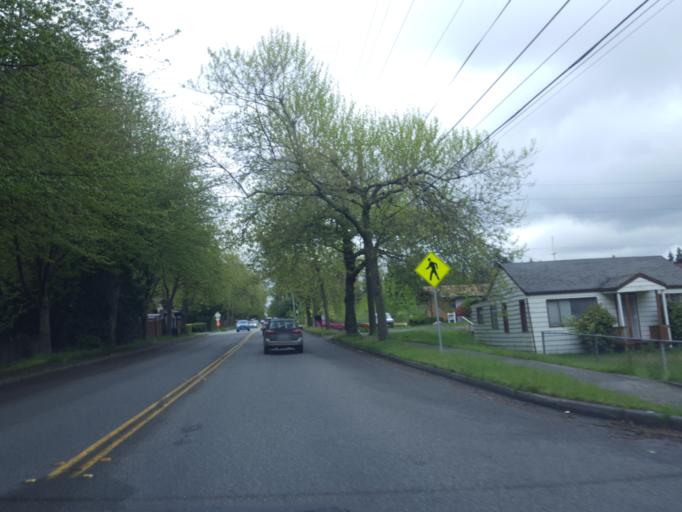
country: US
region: Washington
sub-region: King County
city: Shoreline
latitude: 47.7586
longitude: -122.3349
